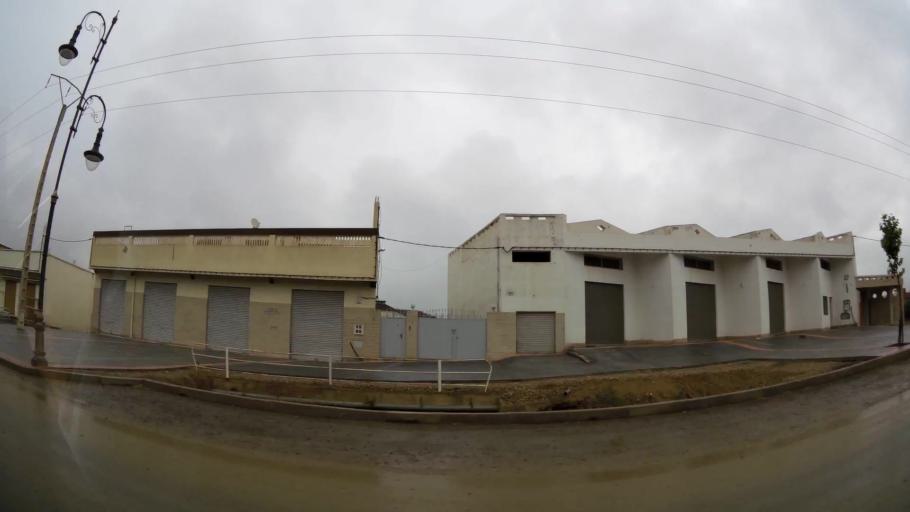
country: MA
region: Taza-Al Hoceima-Taounate
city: Imzourene
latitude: 35.1648
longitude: -3.8563
